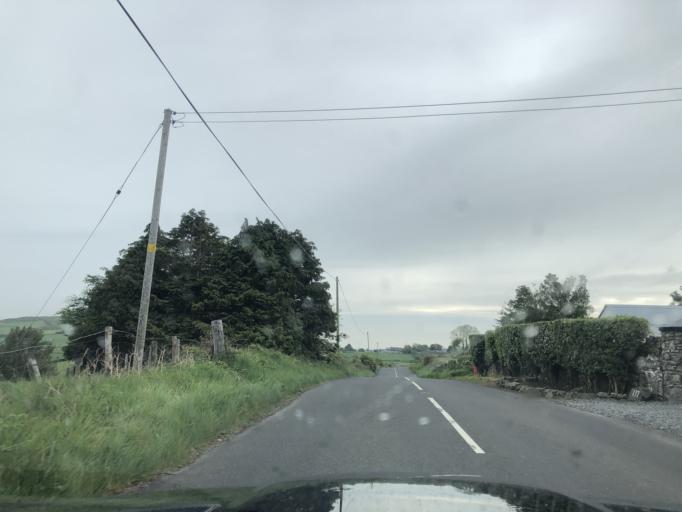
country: GB
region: Northern Ireland
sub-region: Down District
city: Castlewellan
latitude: 54.2219
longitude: -6.0155
